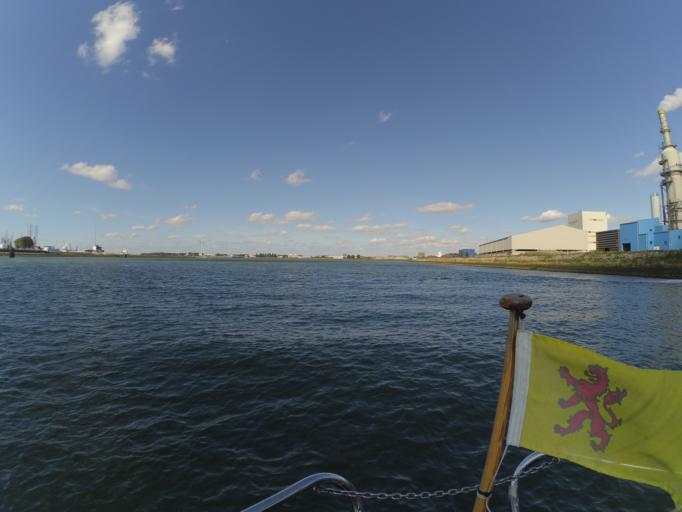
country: NL
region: South Holland
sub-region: Gemeente Vlaardingen
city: Vlaardingen
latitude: 51.8870
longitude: 4.3251
